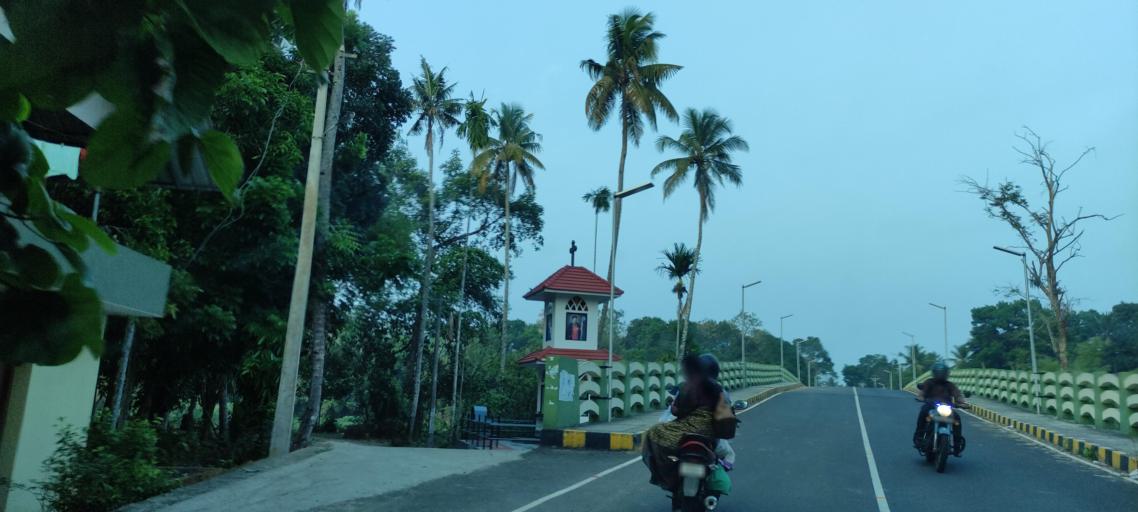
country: IN
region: Kerala
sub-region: Alappuzha
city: Mavelikara
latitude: 9.2703
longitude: 76.5565
